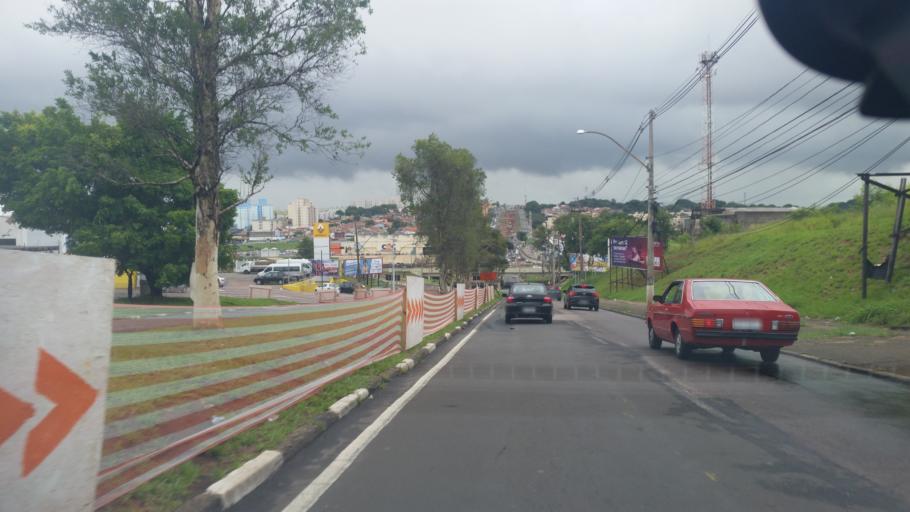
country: BR
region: Sao Paulo
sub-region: Campinas
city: Campinas
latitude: -22.9113
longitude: -47.0976
